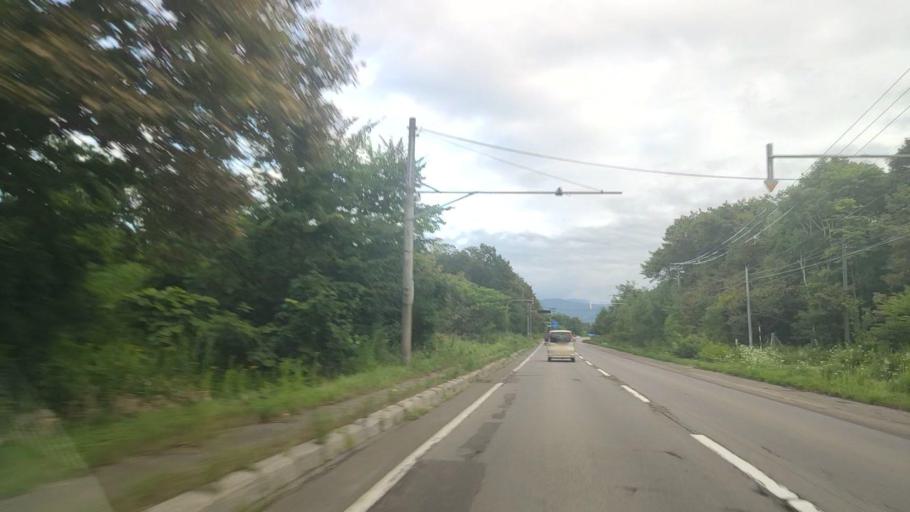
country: JP
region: Hokkaido
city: Nanae
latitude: 42.0119
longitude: 140.6275
